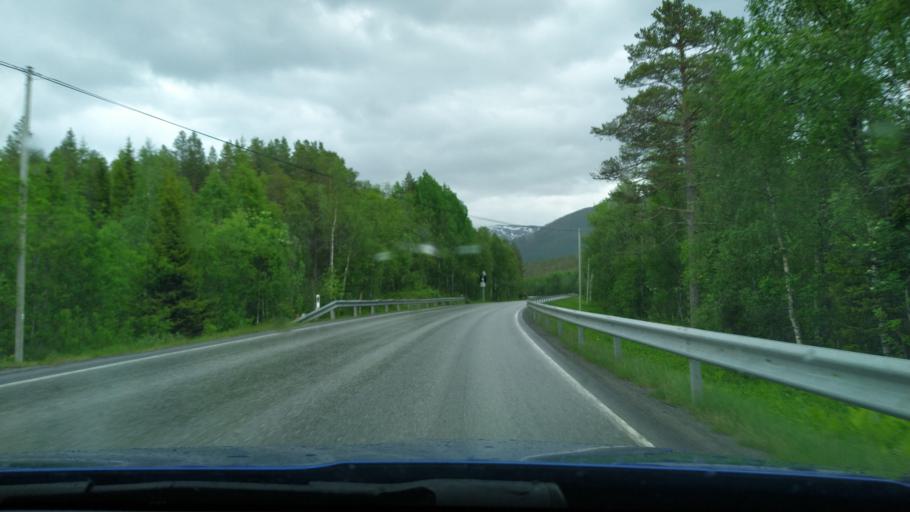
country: NO
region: Troms
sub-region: Malselv
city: Moen
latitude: 69.1341
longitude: 18.6898
